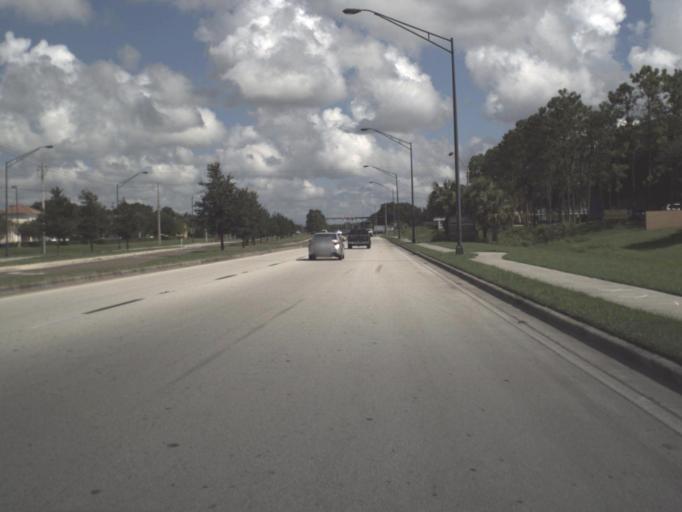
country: US
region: Florida
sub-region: Polk County
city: Medulla
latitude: 27.9996
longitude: -81.9749
